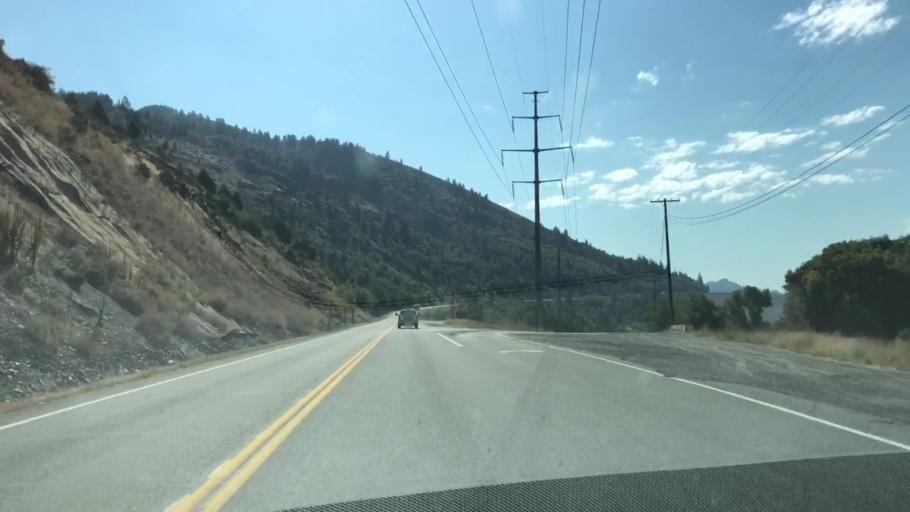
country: US
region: Idaho
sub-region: Teton County
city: Victor
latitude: 43.3457
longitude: -111.2079
